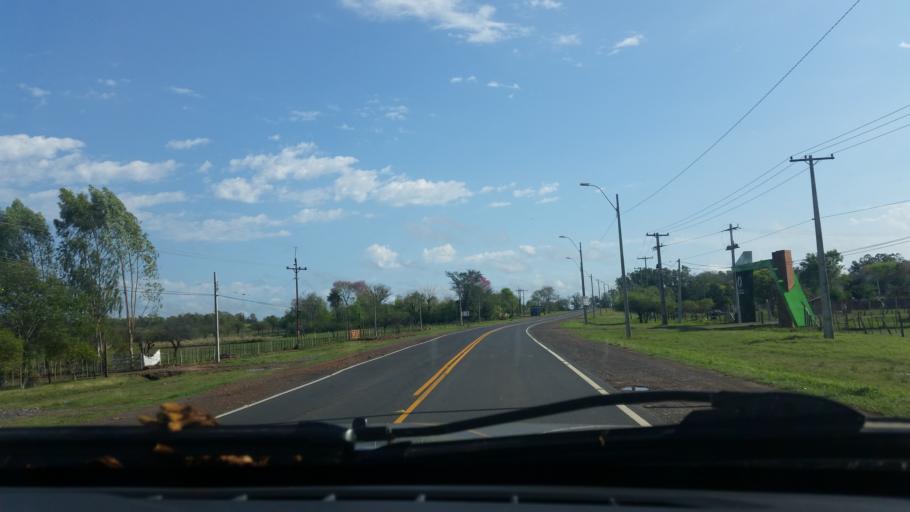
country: PY
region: Presidente Hayes
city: Villa Hayes
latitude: -25.0648
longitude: -57.5339
